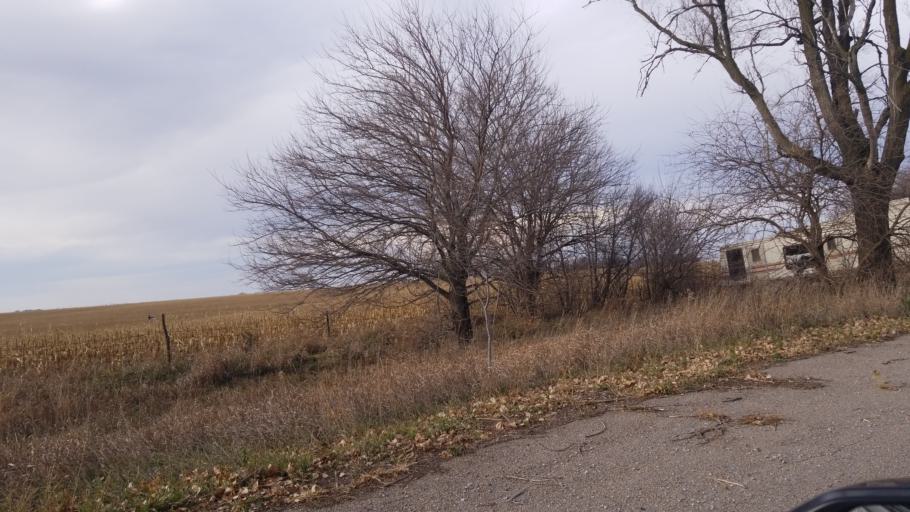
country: US
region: Nebraska
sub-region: Cass County
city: Weeping Water
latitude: 40.8153
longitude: -96.2071
